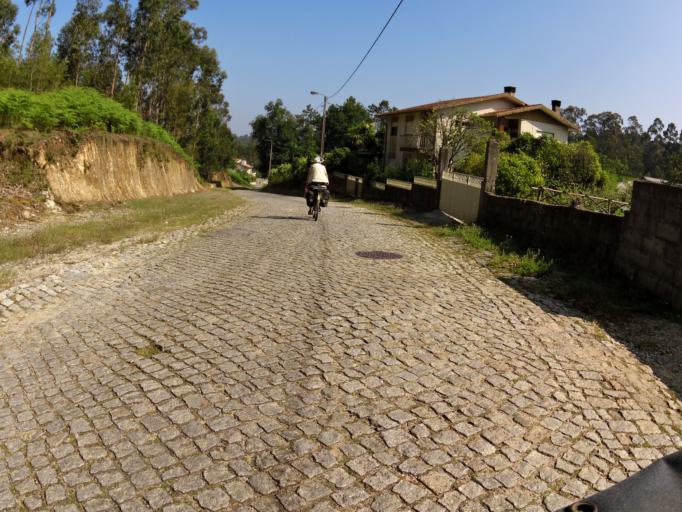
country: PT
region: Porto
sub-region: Vila Nova de Gaia
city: Olival
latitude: 41.0436
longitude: -8.5355
